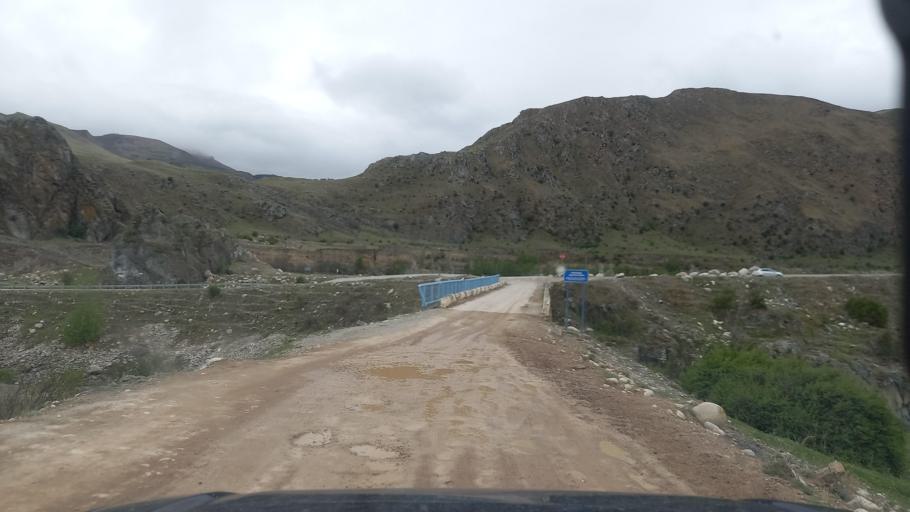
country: RU
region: Kabardino-Balkariya
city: Bylym
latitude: 43.4580
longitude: 43.0134
